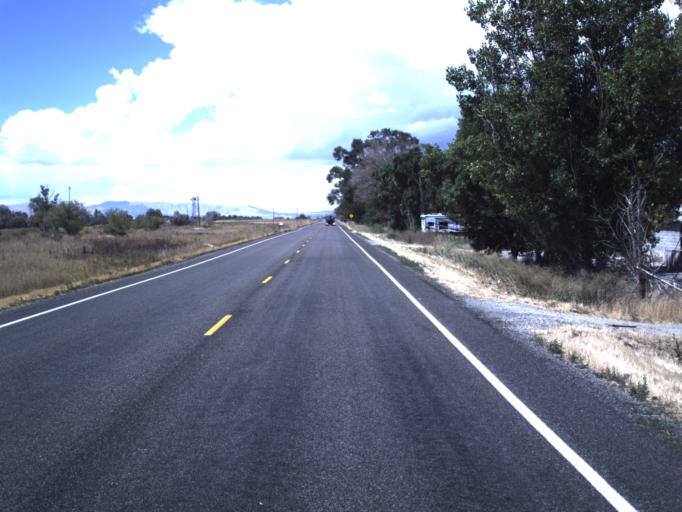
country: US
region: Utah
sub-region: Box Elder County
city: Honeyville
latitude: 41.5606
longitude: -112.1550
